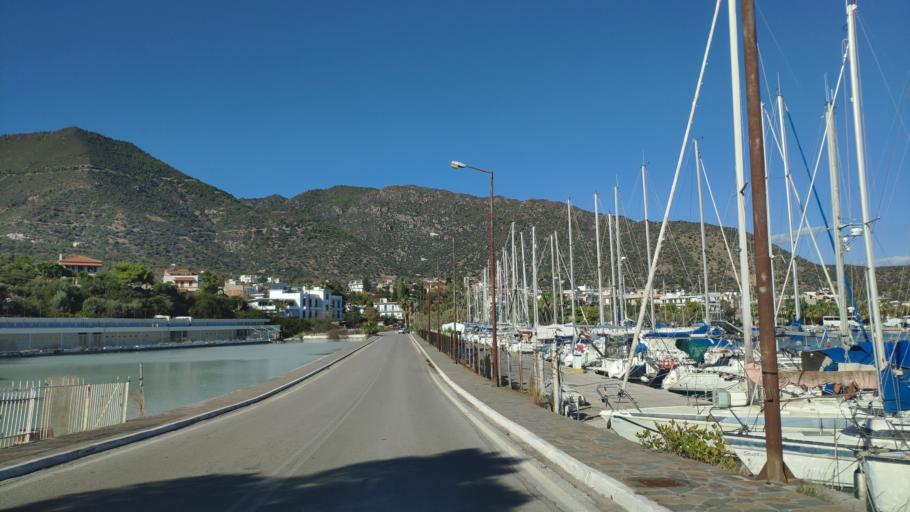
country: GR
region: Attica
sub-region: Nomos Piraios
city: Galatas
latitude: 37.5763
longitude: 23.3879
